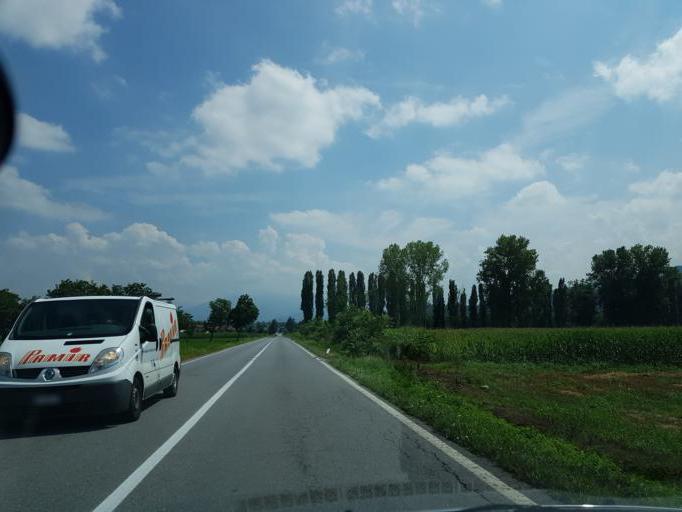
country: IT
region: Piedmont
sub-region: Provincia di Cuneo
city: Bernezzo
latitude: 44.3989
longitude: 7.4505
